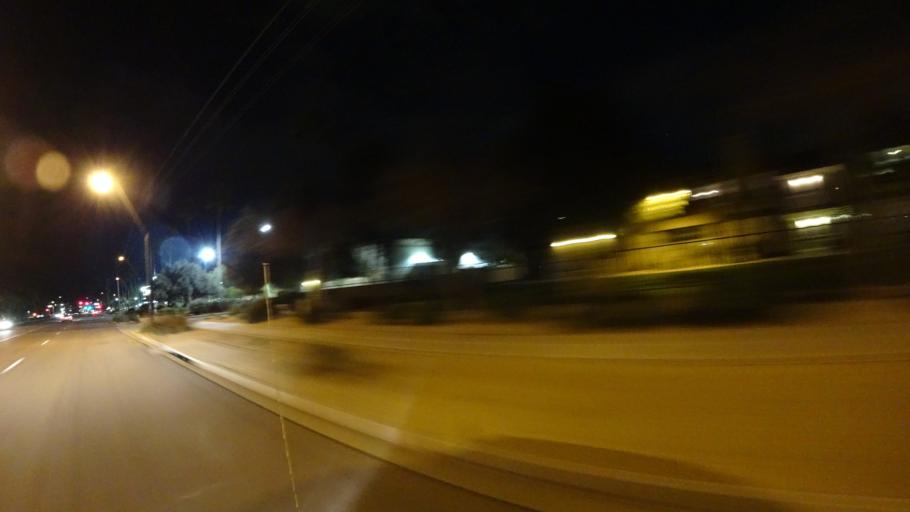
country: US
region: Arizona
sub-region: Maricopa County
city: Guadalupe
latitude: 33.3225
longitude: -111.9632
